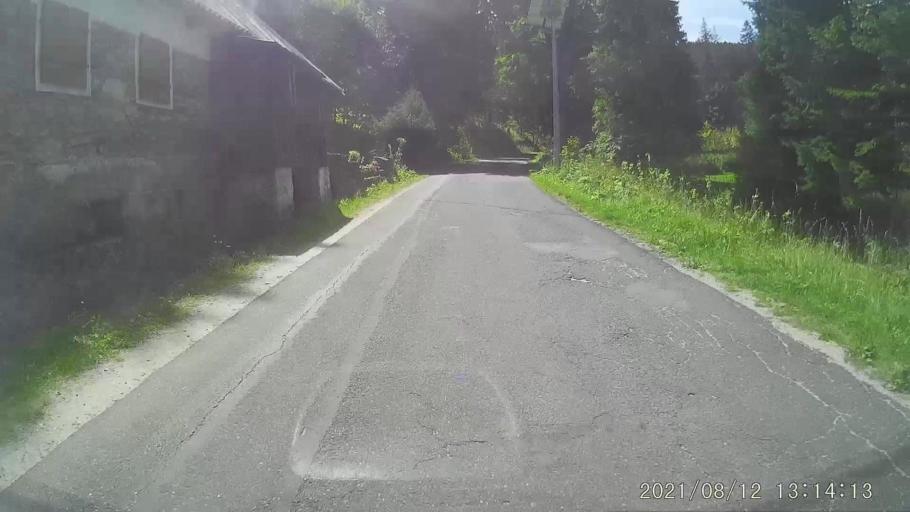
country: PL
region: Lower Silesian Voivodeship
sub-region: Powiat klodzki
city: Stronie Slaskie
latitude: 50.2578
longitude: 16.8583
